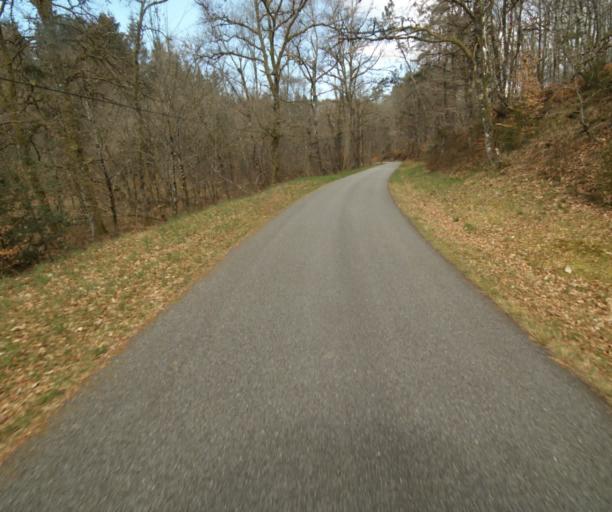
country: FR
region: Limousin
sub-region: Departement de la Correze
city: Laguenne
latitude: 45.2302
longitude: 1.9074
